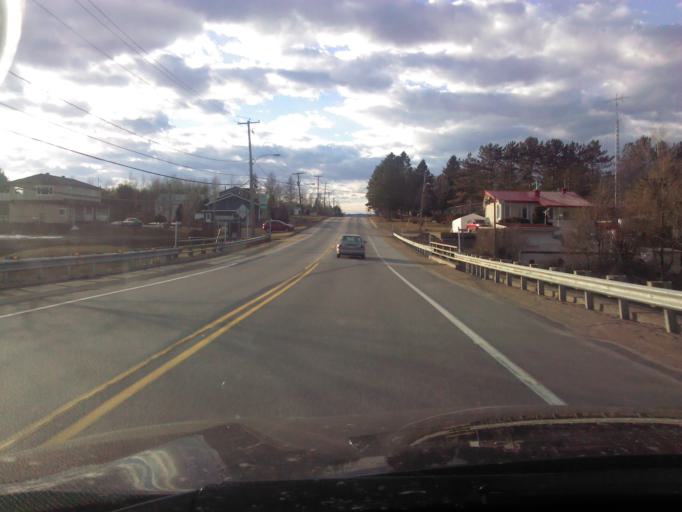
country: CA
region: Quebec
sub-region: Capitale-Nationale
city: Sainte Catherine de la Jacques Cartier
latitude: 46.8127
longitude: -71.5711
